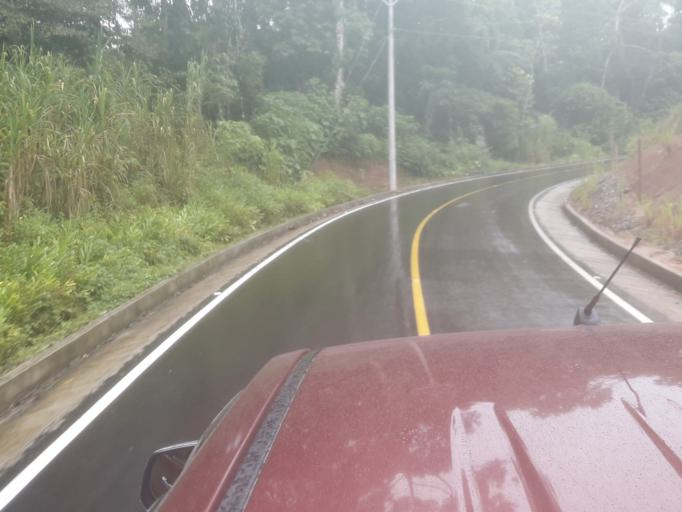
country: EC
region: Napo
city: Tena
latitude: -1.0239
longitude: -77.6643
